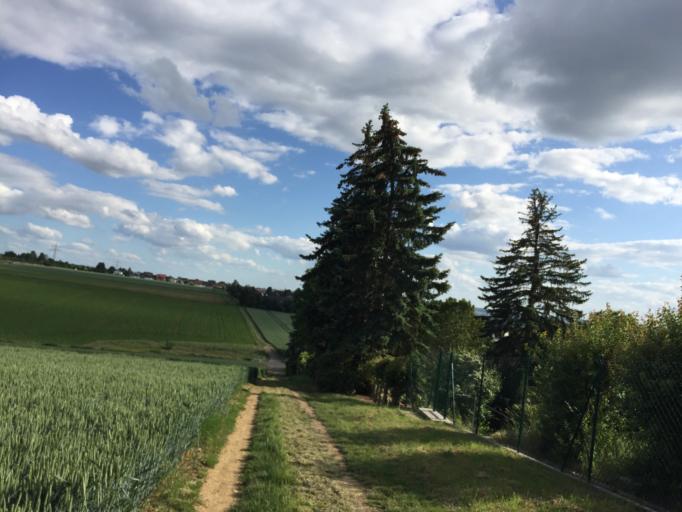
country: DE
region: Hesse
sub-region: Regierungsbezirk Darmstadt
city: Karben
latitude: 50.2316
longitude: 8.7794
